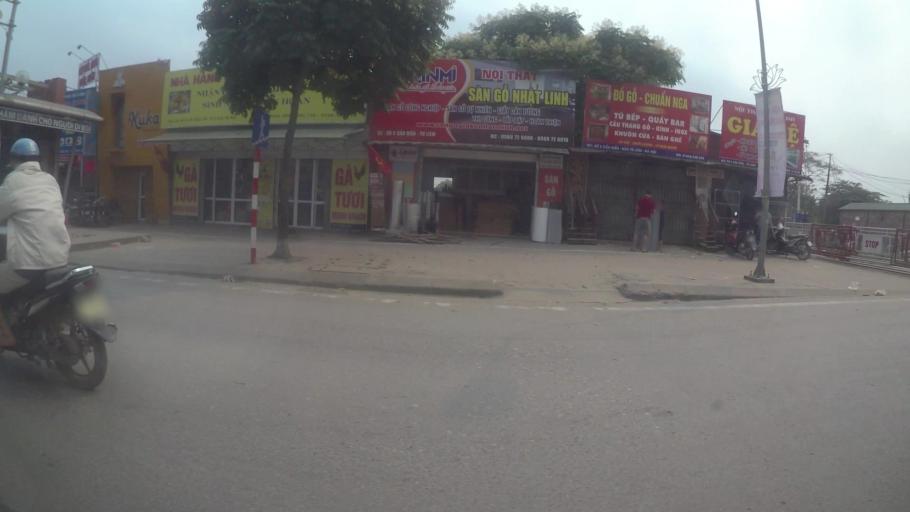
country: VN
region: Ha Noi
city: Cau Dien
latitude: 21.0433
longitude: 105.7566
